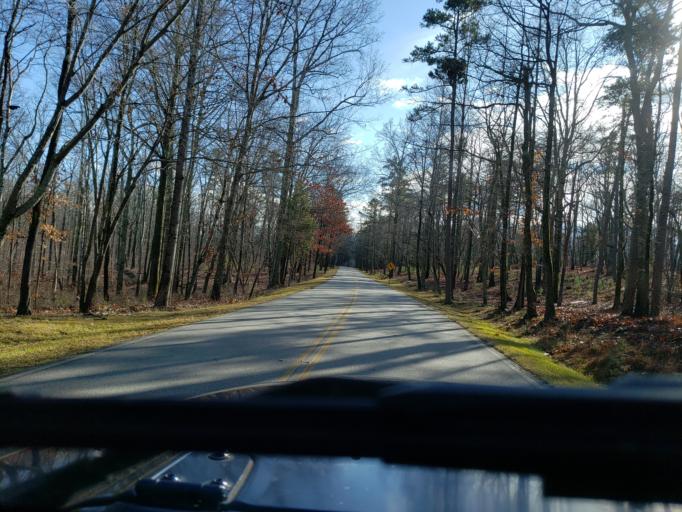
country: US
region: North Carolina
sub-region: Cleveland County
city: White Plains
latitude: 35.1455
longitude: -81.3876
